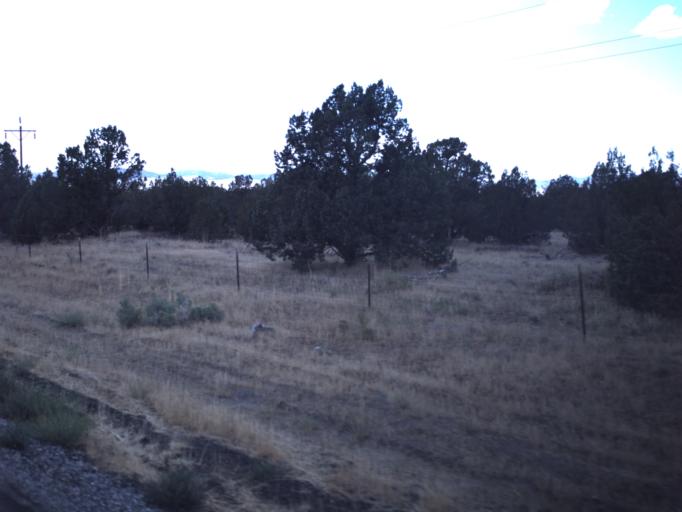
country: US
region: Utah
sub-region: Tooele County
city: Grantsville
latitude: 40.3140
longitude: -112.6342
